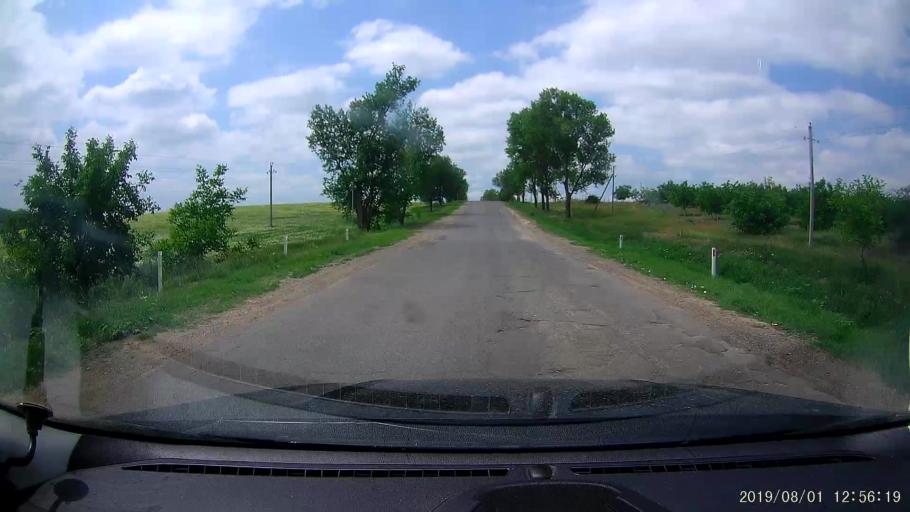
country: MD
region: Gagauzia
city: Vulcanesti
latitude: 45.6921
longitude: 28.4488
